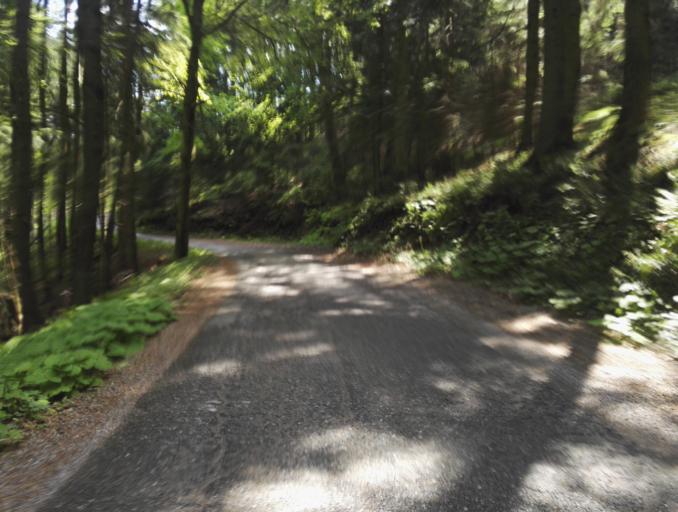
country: AT
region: Styria
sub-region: Politischer Bezirk Graz-Umgebung
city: Sankt Radegund bei Graz
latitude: 47.2021
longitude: 15.4485
